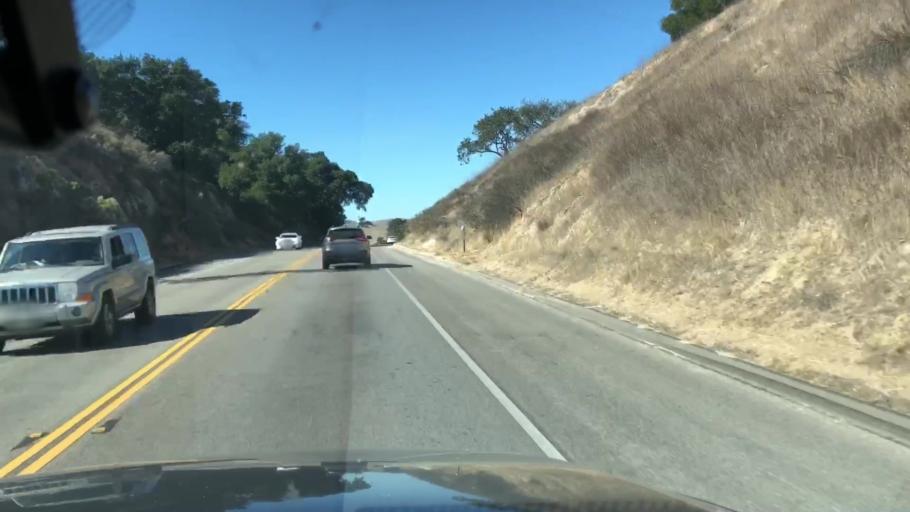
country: US
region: California
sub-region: Santa Barbara County
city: Los Olivos
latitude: 34.6770
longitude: -120.1342
